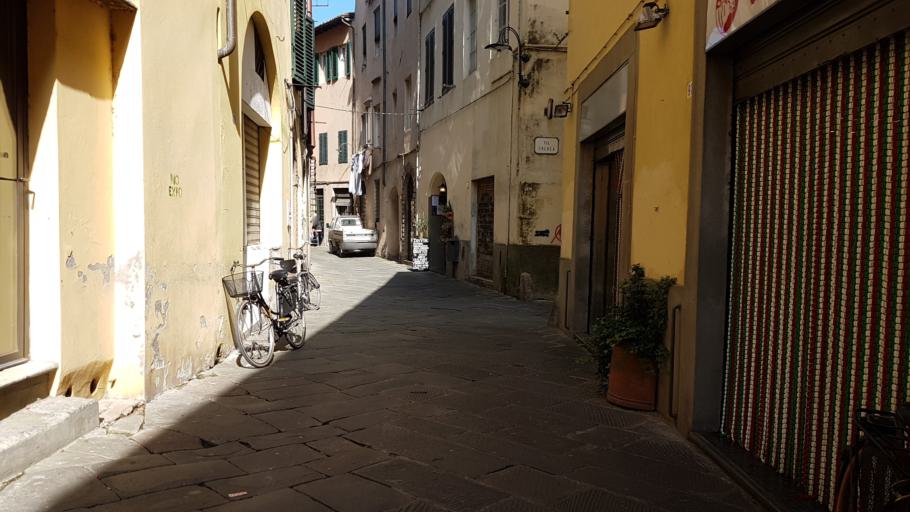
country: IT
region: Tuscany
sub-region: Provincia di Lucca
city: Lucca
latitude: 43.8451
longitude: 10.5060
